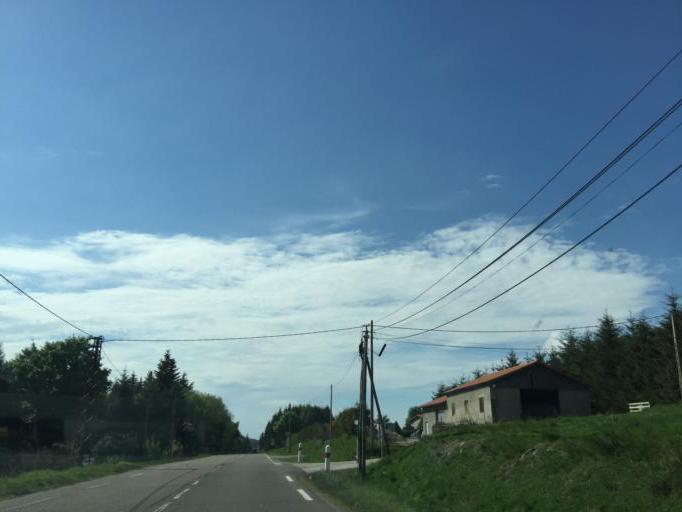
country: FR
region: Rhone-Alpes
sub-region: Departement de la Loire
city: Saint-Genest-Malifaux
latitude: 45.3530
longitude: 4.4696
